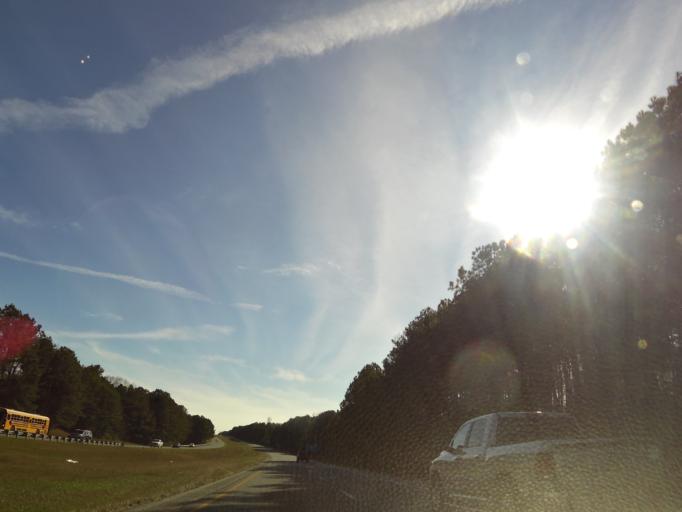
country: US
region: Alabama
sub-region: Russell County
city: Phenix City
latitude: 32.5831
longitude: -84.9609
